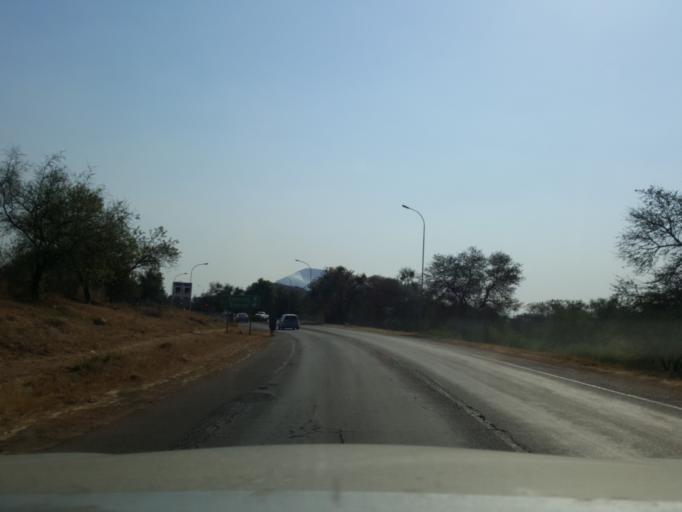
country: BW
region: South East
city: Lobatse
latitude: -25.2269
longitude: 25.6760
